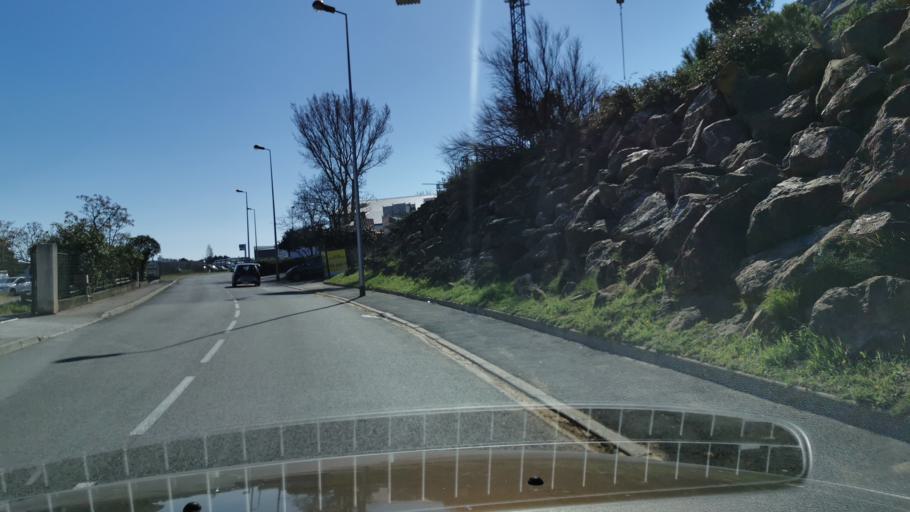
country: FR
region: Languedoc-Roussillon
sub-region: Departement de l'Aude
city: Narbonne
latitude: 43.1564
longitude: 2.9781
